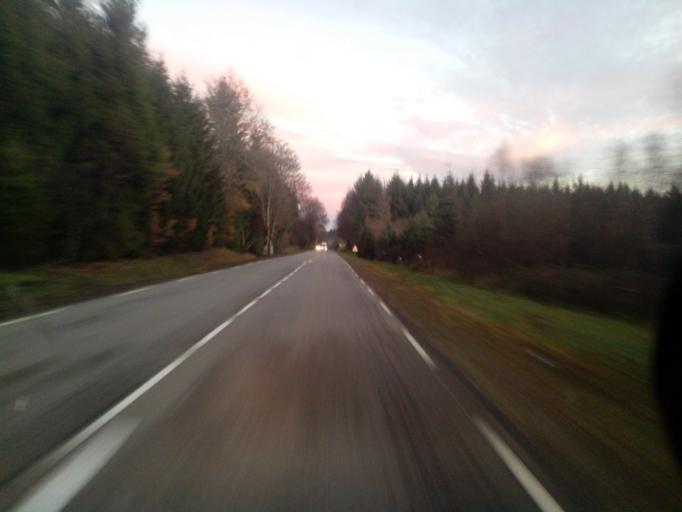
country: FR
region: Limousin
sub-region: Departement de la Correze
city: Meymac
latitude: 45.5068
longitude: 2.2060
